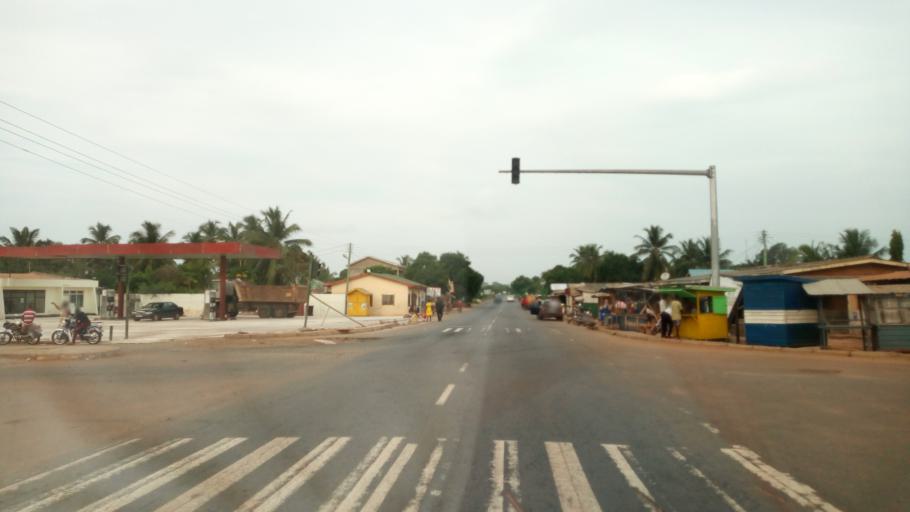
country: GH
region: Volta
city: Keta
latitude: 6.0527
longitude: 0.9761
